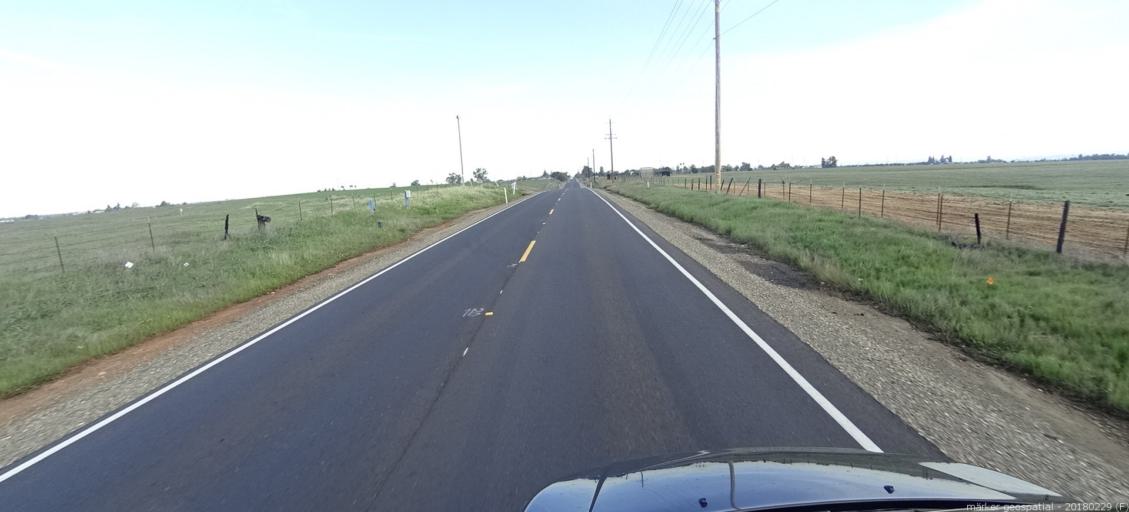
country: US
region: California
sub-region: Sacramento County
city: Vineyard
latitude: 38.5008
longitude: -121.2979
